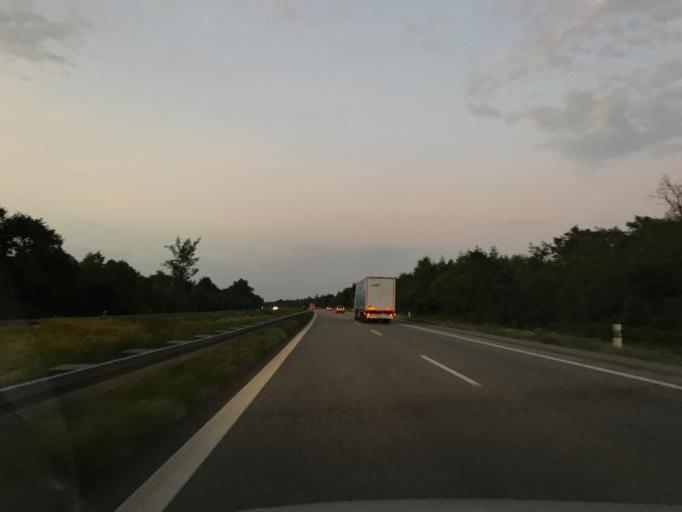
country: FR
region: Alsace
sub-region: Departement du Haut-Rhin
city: Blodelsheim
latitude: 47.8679
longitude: 7.5671
